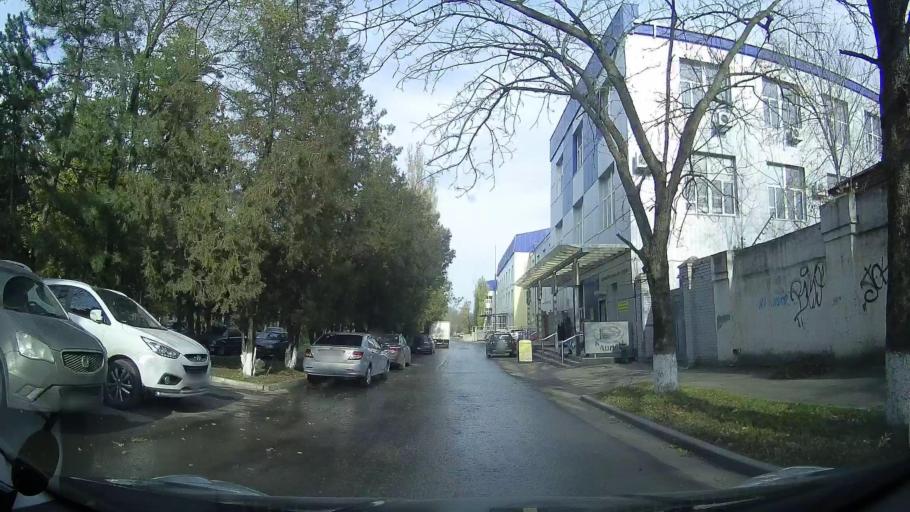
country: RU
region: Rostov
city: Severnyy
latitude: 47.2663
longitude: 39.7232
